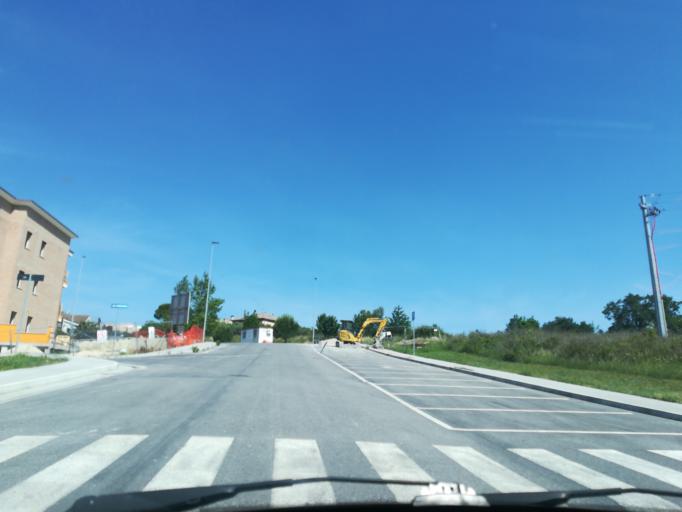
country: IT
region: The Marches
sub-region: Provincia di Macerata
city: Piediripa
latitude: 43.2894
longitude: 13.4767
